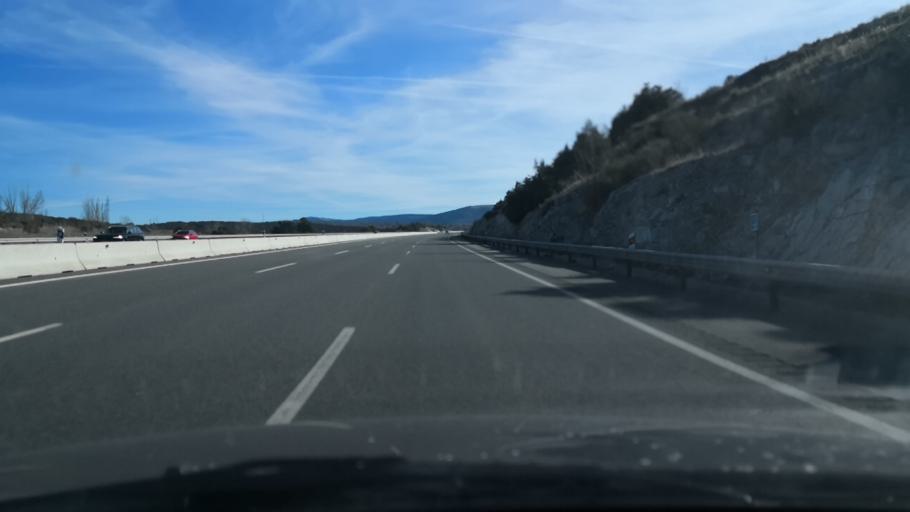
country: ES
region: Castille and Leon
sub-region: Provincia de Segovia
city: Ituero y Lama
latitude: 40.7646
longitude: -4.3740
